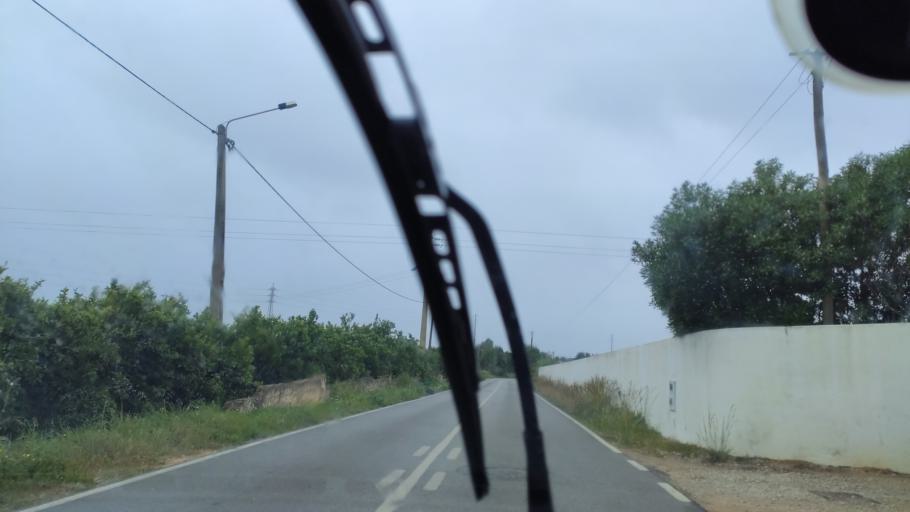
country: PT
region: Faro
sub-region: Faro
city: Santa Barbara de Nexe
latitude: 37.0739
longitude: -7.9452
